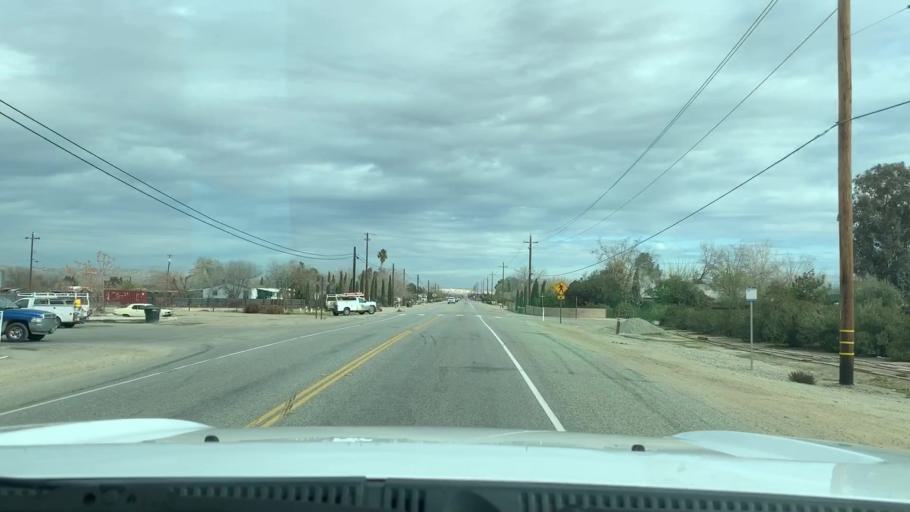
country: US
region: California
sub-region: Kern County
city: Ford City
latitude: 35.2070
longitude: -119.4090
